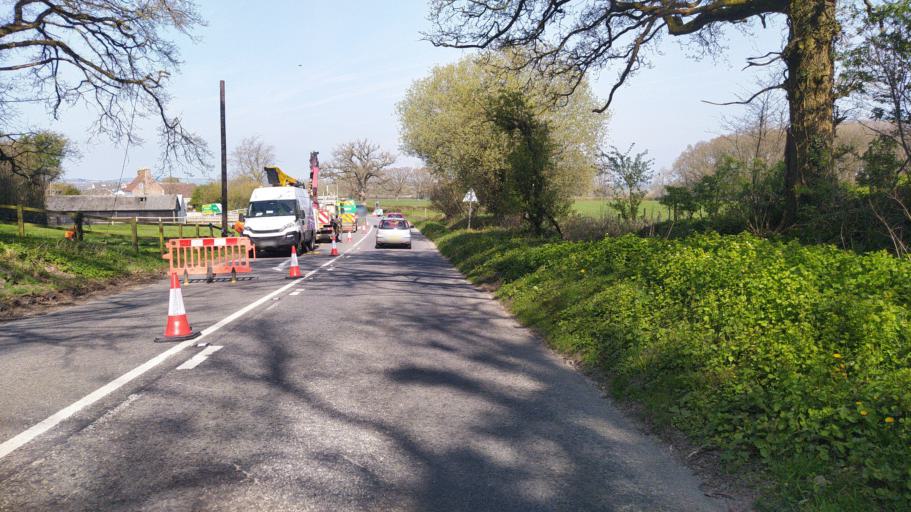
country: GB
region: England
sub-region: Wiltshire
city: Corsley
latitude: 51.2126
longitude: -2.2736
